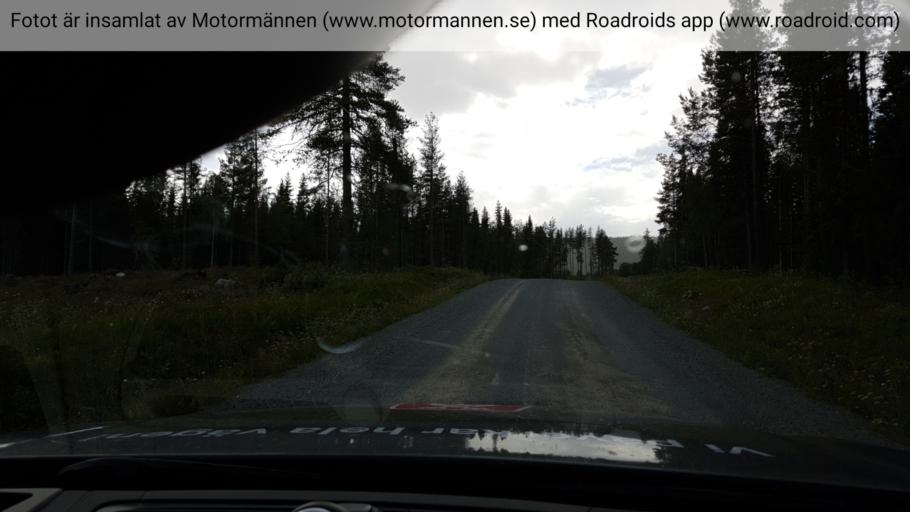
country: SE
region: Jaemtland
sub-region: Bergs Kommun
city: Hoverberg
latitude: 62.9614
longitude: 14.2491
